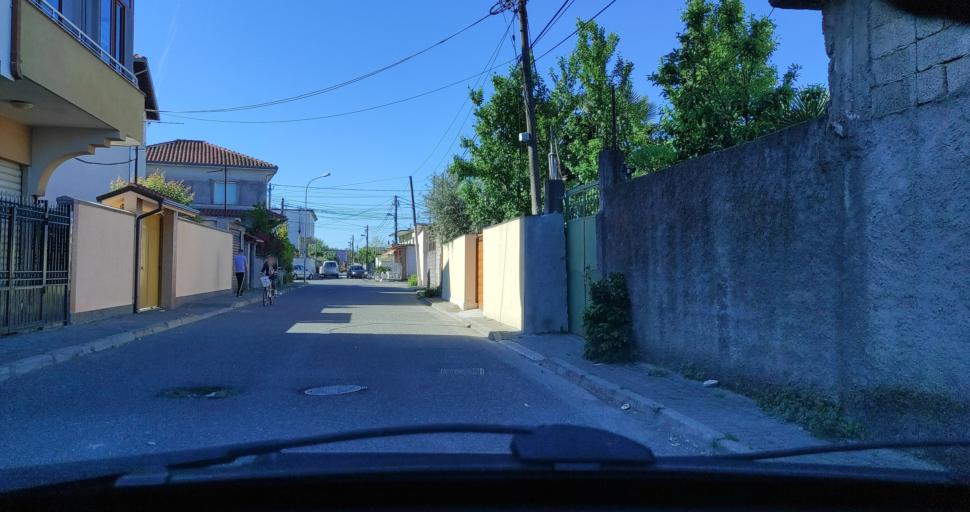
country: AL
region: Shkoder
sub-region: Rrethi i Shkodres
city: Shkoder
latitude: 42.0741
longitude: 19.5016
